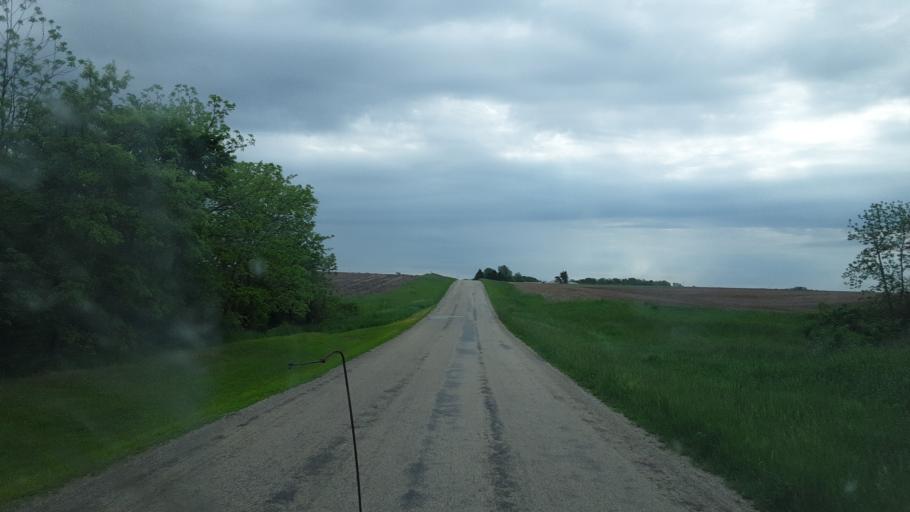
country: US
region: Illinois
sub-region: Fulton County
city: Astoria
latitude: 40.3645
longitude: -90.4665
